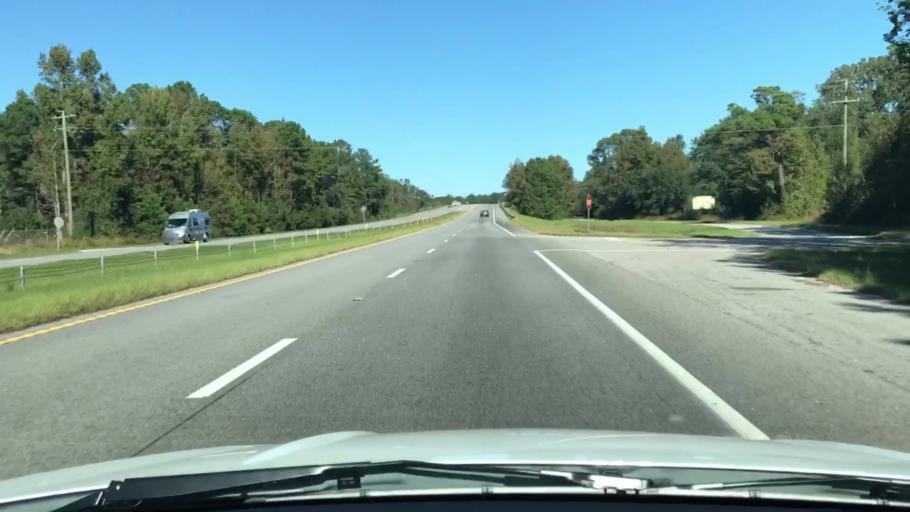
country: US
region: South Carolina
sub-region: Colleton County
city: Walterboro
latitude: 32.7310
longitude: -80.5961
